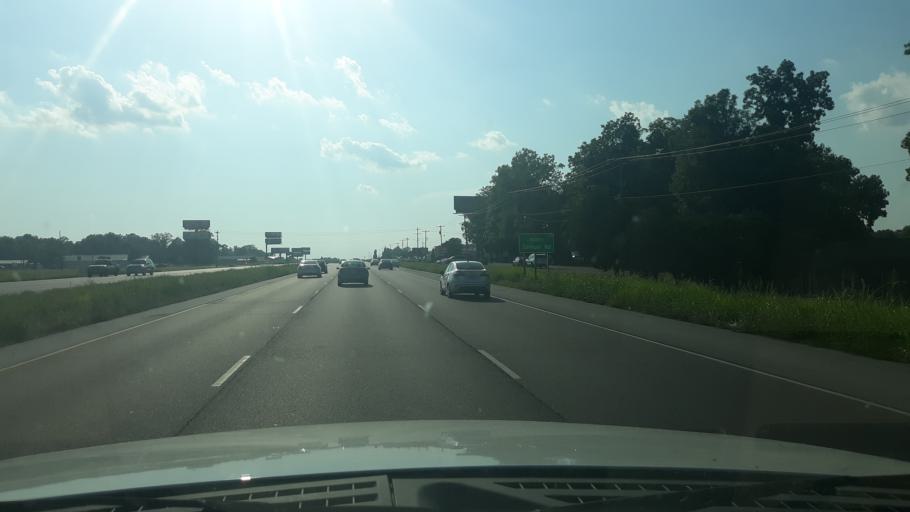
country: US
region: Illinois
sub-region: Williamson County
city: Crainville
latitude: 37.7451
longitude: -89.0412
